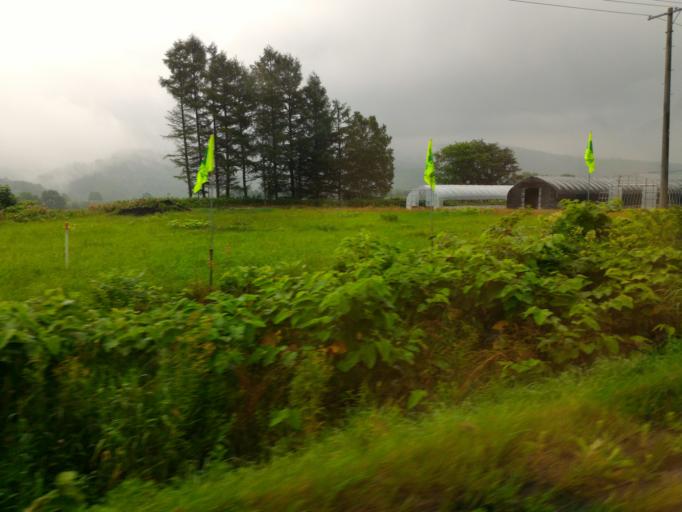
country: JP
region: Hokkaido
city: Nayoro
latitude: 44.5889
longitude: 142.3058
